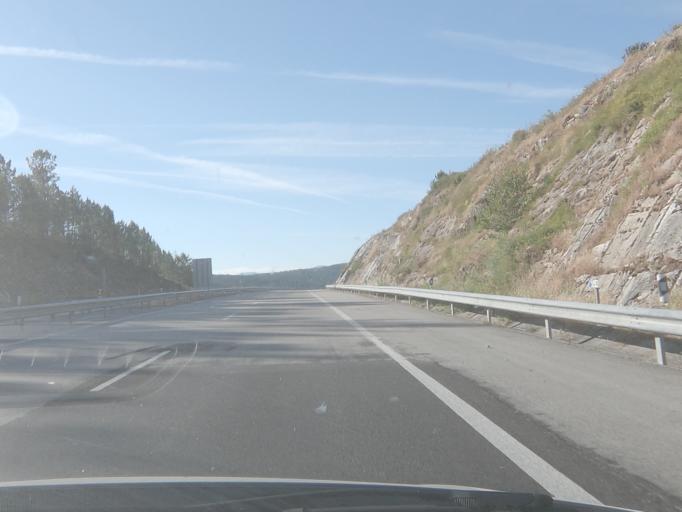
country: PT
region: Viseu
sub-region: Castro Daire
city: Castro Daire
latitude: 40.8294
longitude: -7.9365
